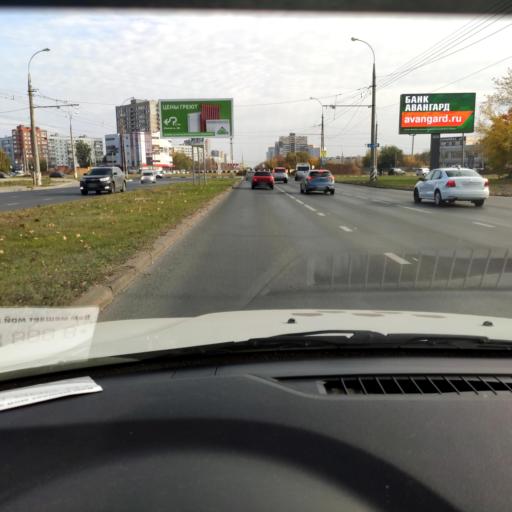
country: RU
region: Samara
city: Tol'yatti
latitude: 53.5238
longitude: 49.3245
